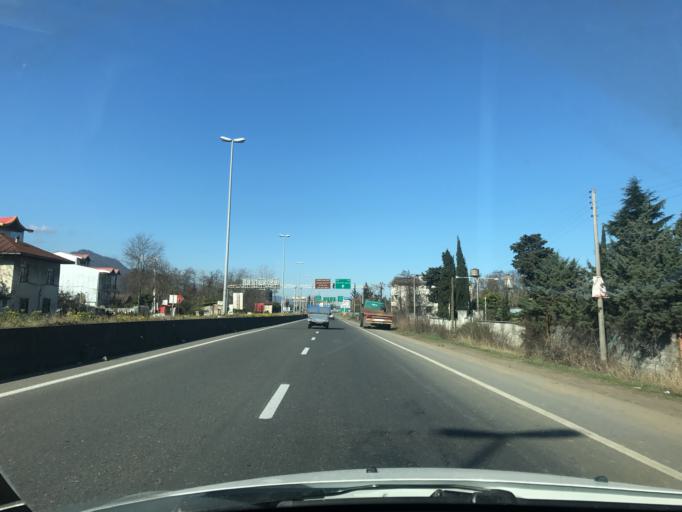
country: IR
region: Mazandaran
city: Ramsar
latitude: 36.9611
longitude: 50.5978
